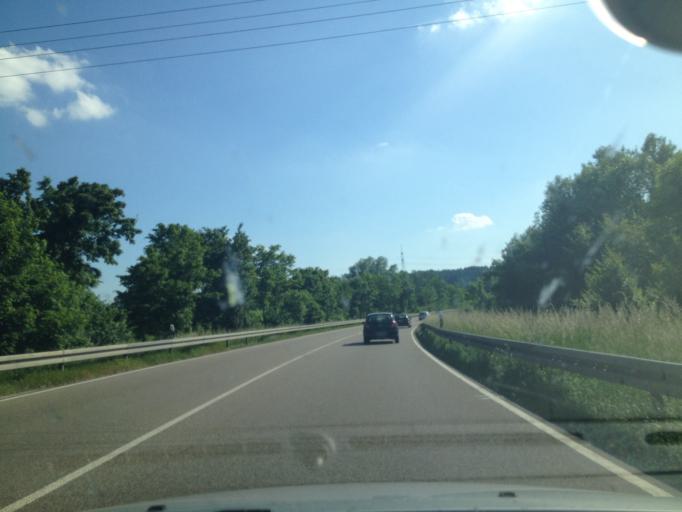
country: DE
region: Bavaria
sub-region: Swabia
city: Aichach
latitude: 48.4404
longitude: 11.1424
